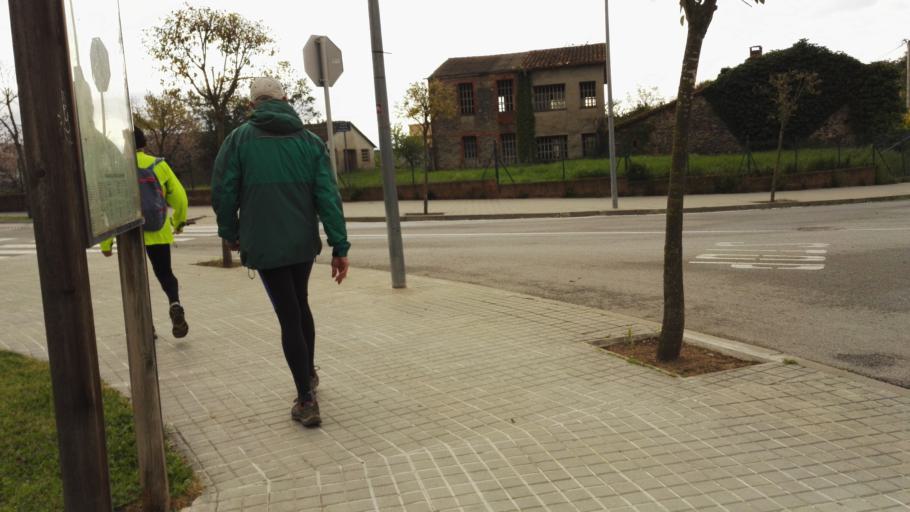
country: ES
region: Catalonia
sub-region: Provincia de Barcelona
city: Santa Maria de Palautordera
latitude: 41.7084
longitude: 2.4306
